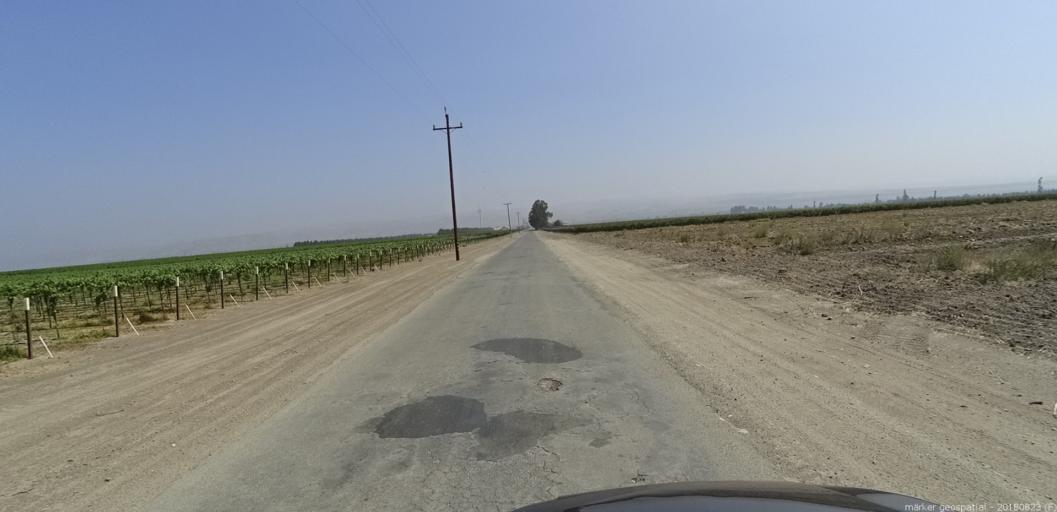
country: US
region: California
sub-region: Monterey County
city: Greenfield
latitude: 36.2640
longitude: -121.2070
